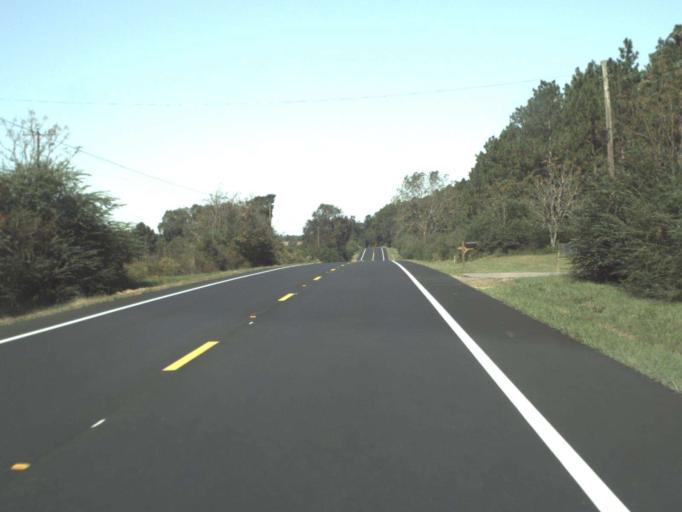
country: US
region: Alabama
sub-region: Covington County
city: Florala
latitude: 30.8657
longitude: -86.2537
